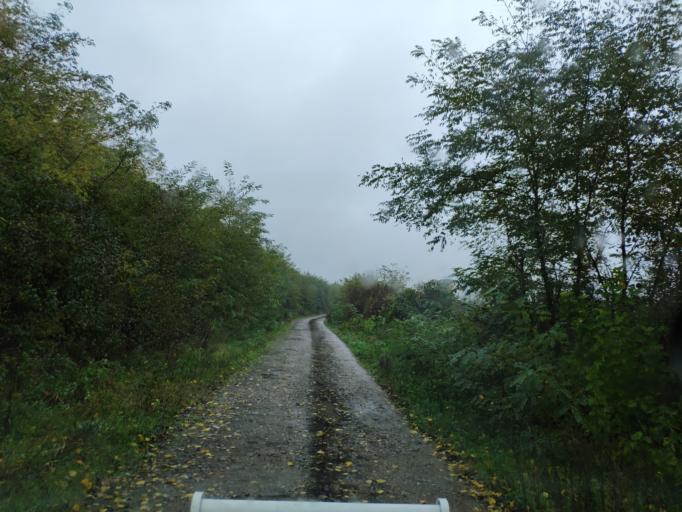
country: SK
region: Kosicky
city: Cierna nad Tisou
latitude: 48.4453
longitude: 21.9987
